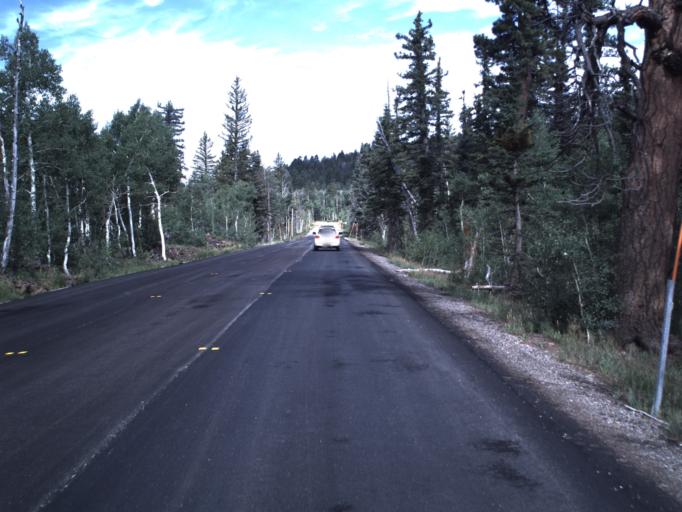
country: US
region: Utah
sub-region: Iron County
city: Parowan
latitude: 37.5172
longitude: -112.7006
